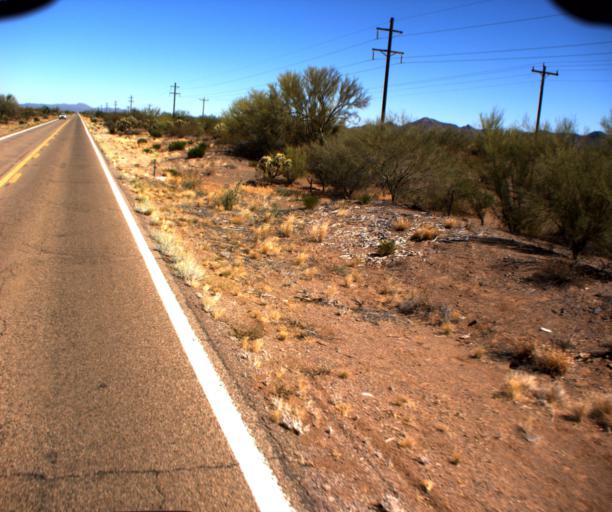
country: US
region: Arizona
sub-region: Pima County
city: Sells
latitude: 31.9944
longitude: -111.9807
